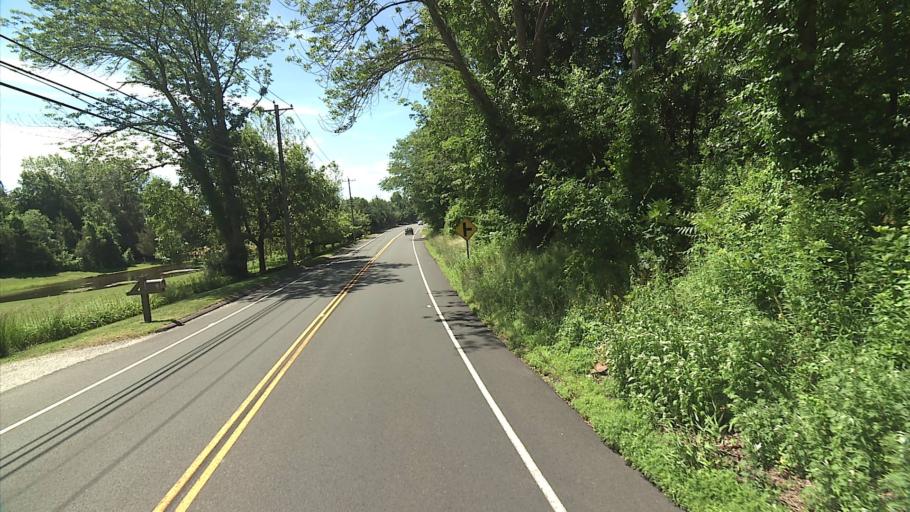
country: US
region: Connecticut
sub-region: New Haven County
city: Guilford
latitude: 41.3009
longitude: -72.6871
